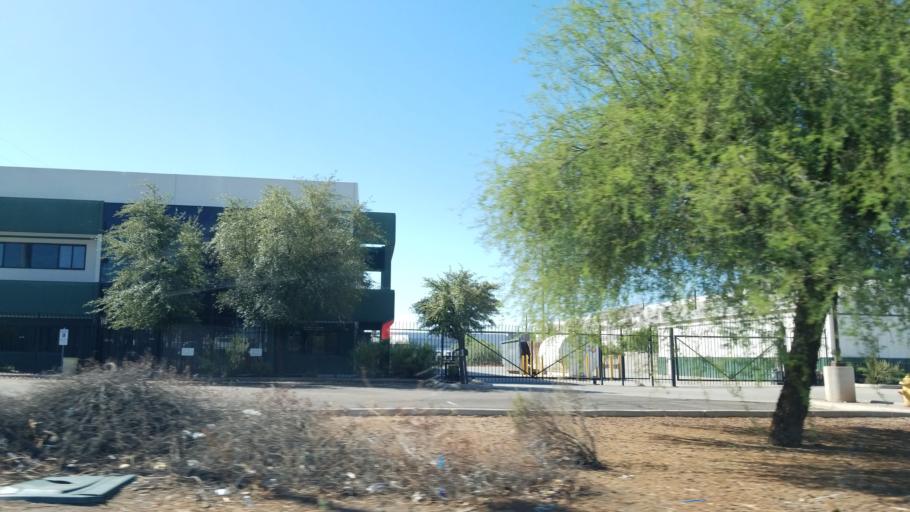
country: US
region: Arizona
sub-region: Maricopa County
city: Laveen
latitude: 33.4367
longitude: -112.1613
